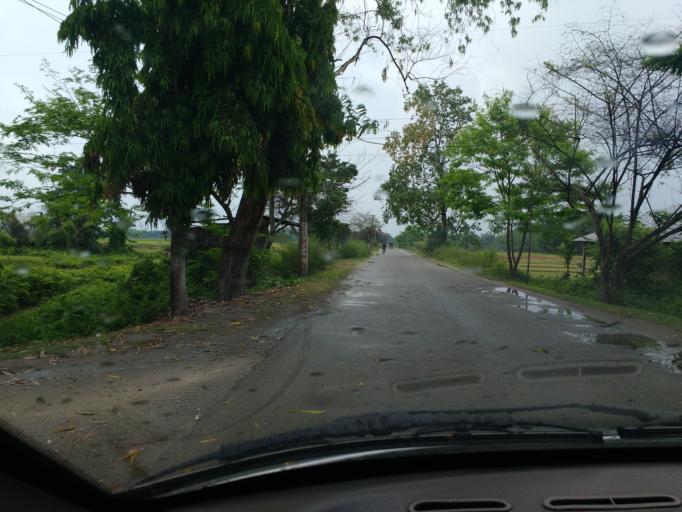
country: IN
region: Assam
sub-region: Udalguri
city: Udalguri
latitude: 26.7223
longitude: 92.2098
